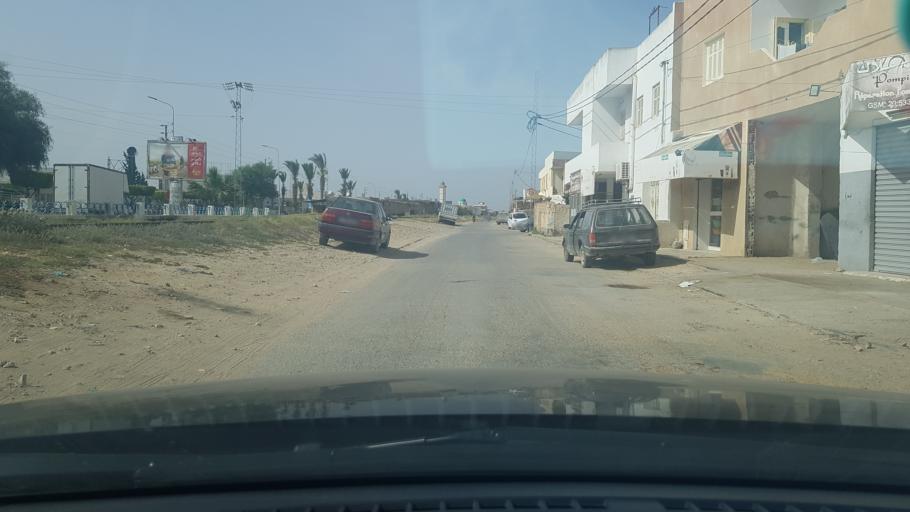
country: TN
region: Safaqis
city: Al Qarmadah
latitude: 34.8181
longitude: 10.7626
